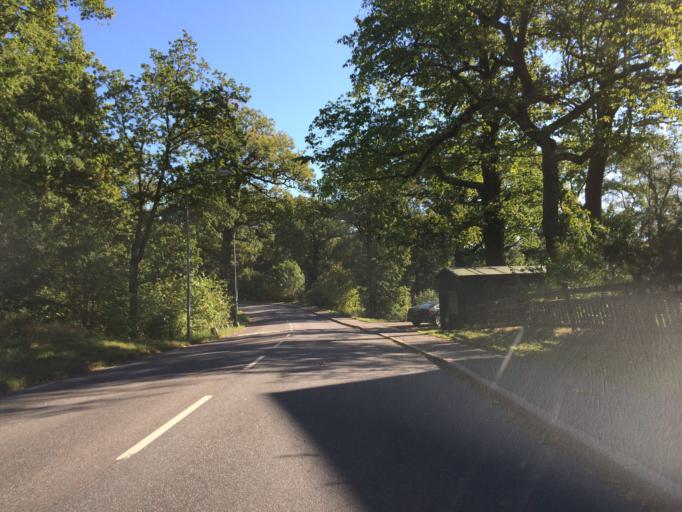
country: SE
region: Stockholm
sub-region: Nacka Kommun
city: Nacka
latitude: 59.3229
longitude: 18.1389
